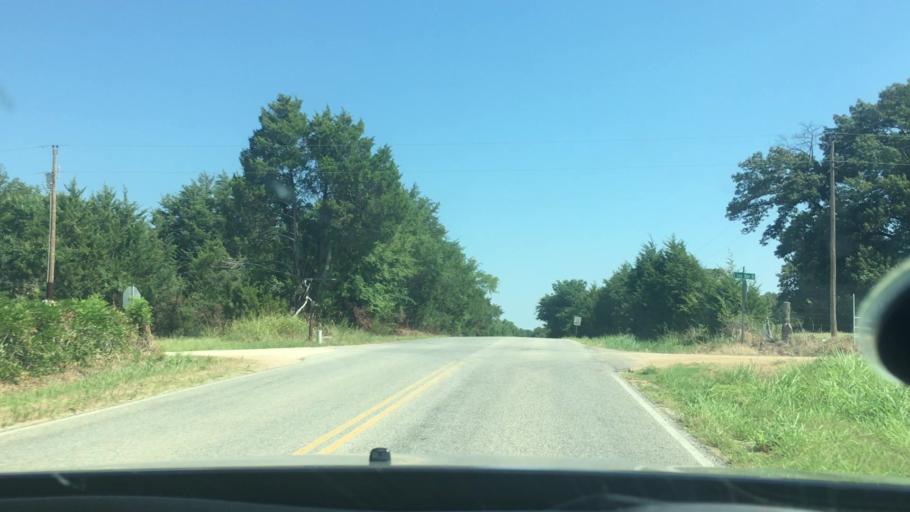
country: US
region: Oklahoma
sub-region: Johnston County
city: Tishomingo
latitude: 34.2593
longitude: -96.6186
